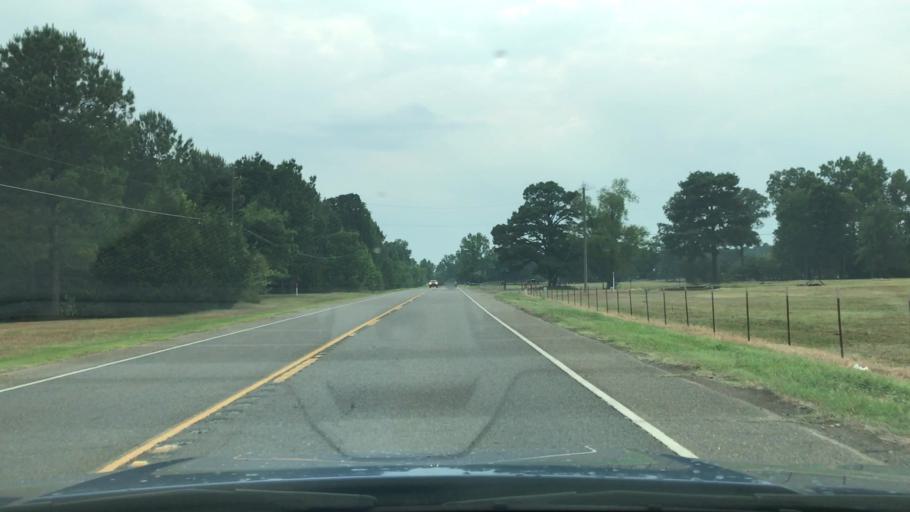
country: US
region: Texas
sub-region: Harrison County
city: Waskom
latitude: 32.4627
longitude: -94.0303
